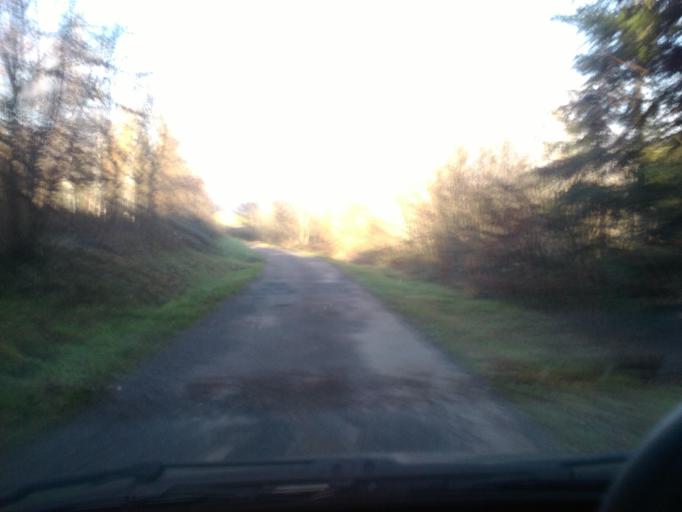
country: FR
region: Lorraine
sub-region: Departement des Vosges
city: Saint-Die-des-Vosges
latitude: 48.3321
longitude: 6.9690
